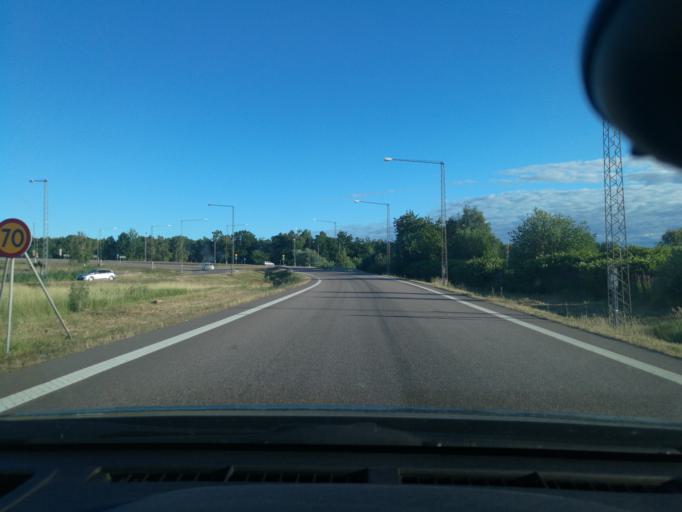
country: SE
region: Kalmar
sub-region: Kalmar Kommun
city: Kalmar
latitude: 56.6847
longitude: 16.3244
